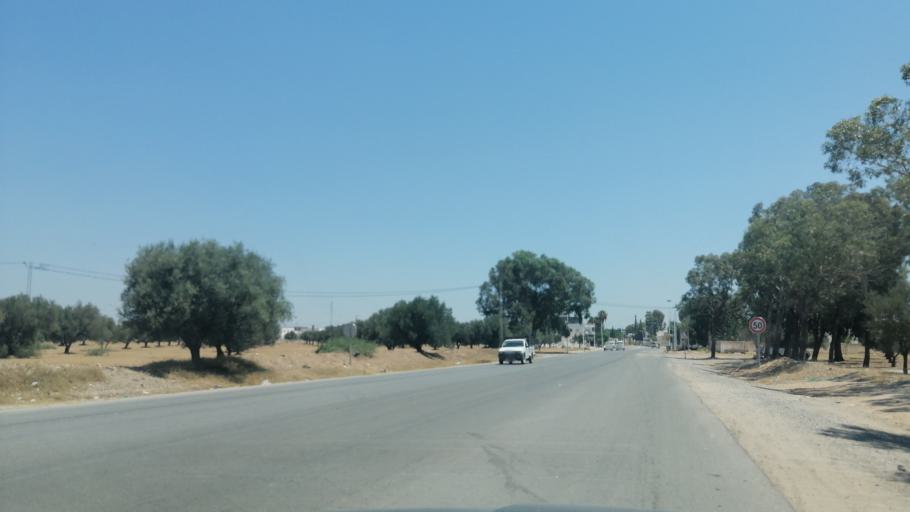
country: TN
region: Al Qayrawan
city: Sbikha
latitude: 36.1209
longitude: 10.0862
